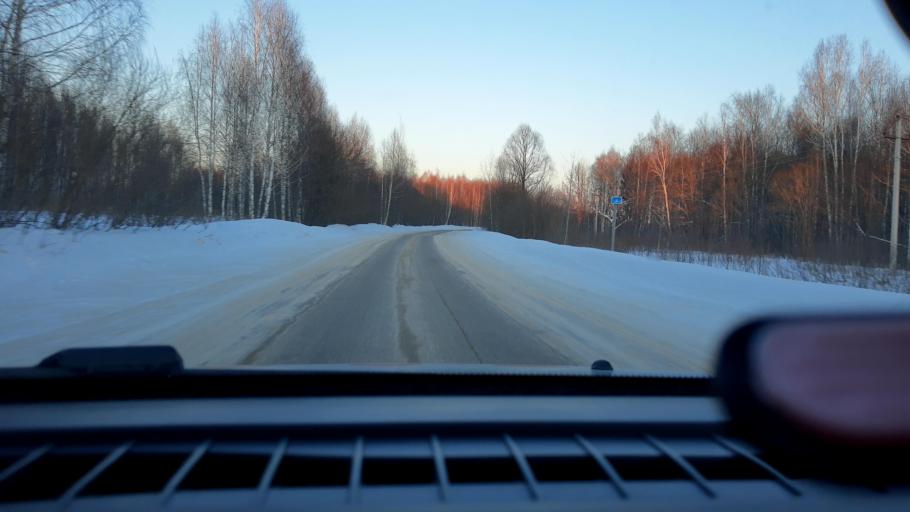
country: RU
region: Nizjnij Novgorod
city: Lyskovo
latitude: 56.1353
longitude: 45.0073
